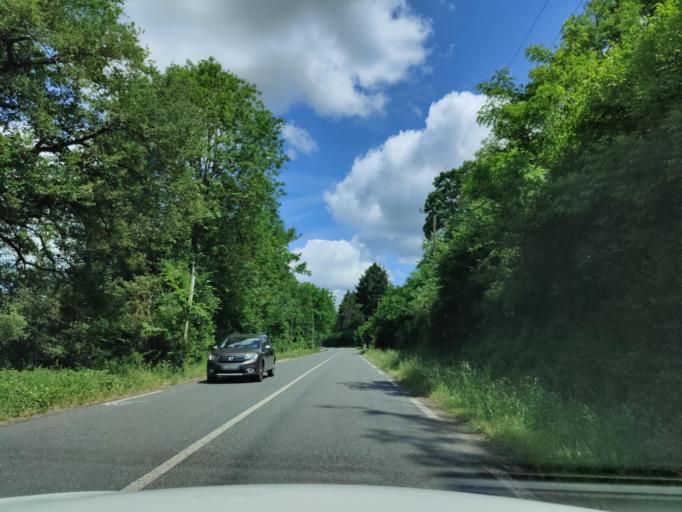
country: FR
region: Auvergne
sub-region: Departement de l'Allier
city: Vallon-en-Sully
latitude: 46.6306
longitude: 2.5932
